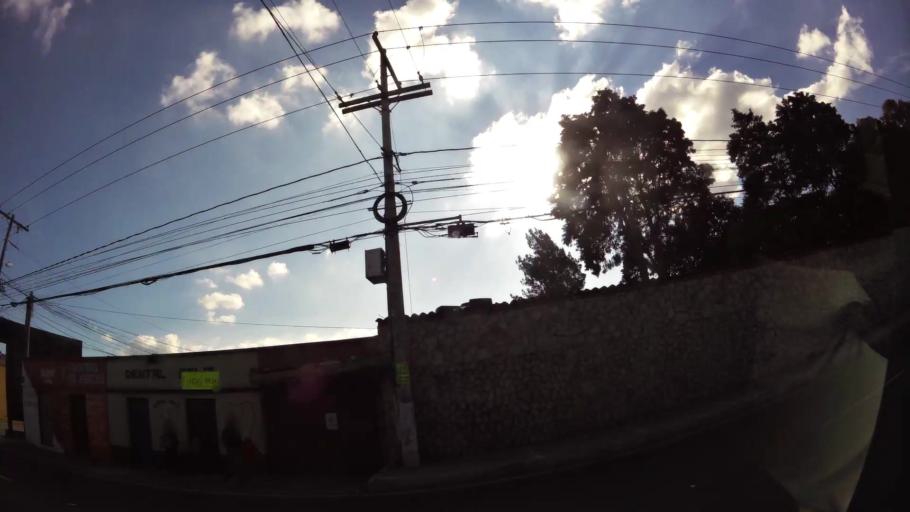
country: GT
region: Guatemala
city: Villa Nueva
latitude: 14.5171
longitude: -90.5787
